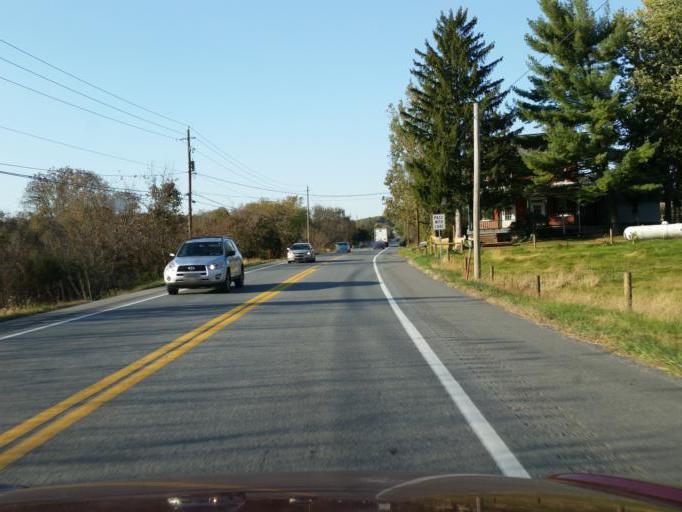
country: US
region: Pennsylvania
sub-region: Lancaster County
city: Elizabethtown
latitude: 40.2005
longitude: -76.6106
